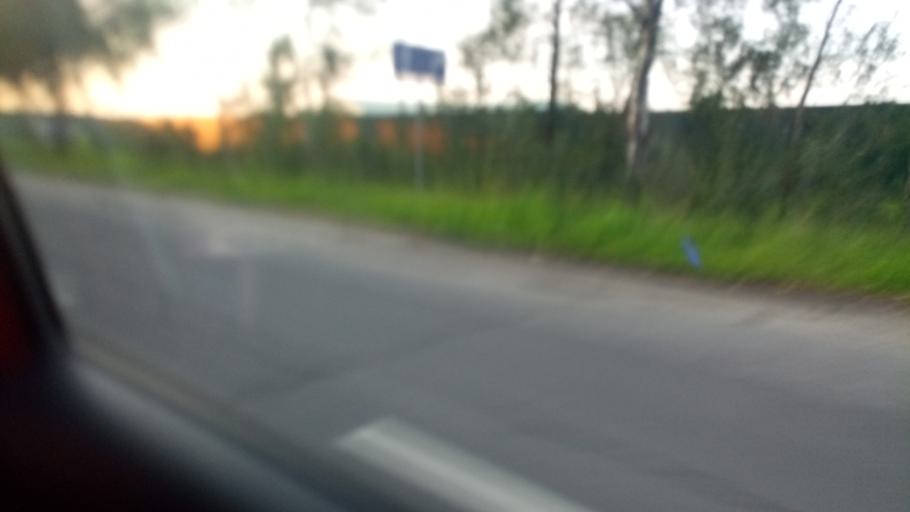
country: RU
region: Moskovskaya
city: Noginsk-9
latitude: 56.0488
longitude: 38.4597
